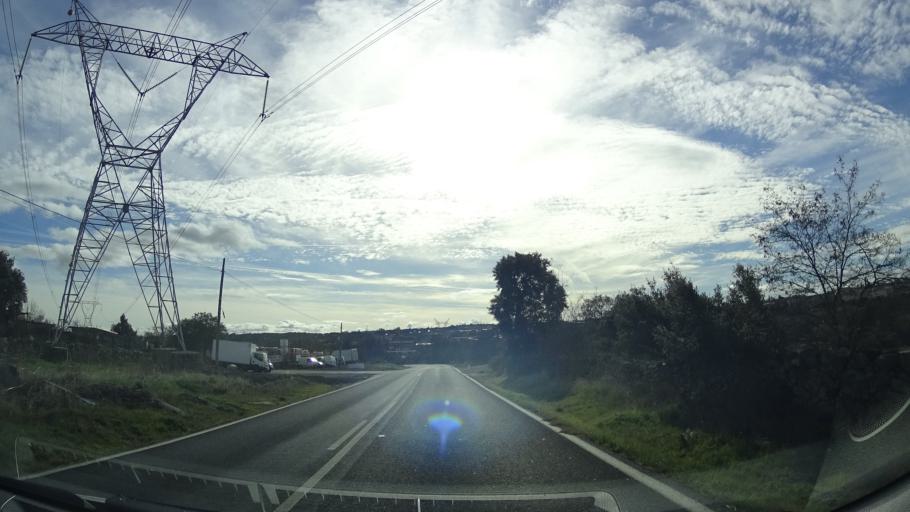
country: ES
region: Madrid
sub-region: Provincia de Madrid
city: Galapagar
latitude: 40.5886
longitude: -4.0028
